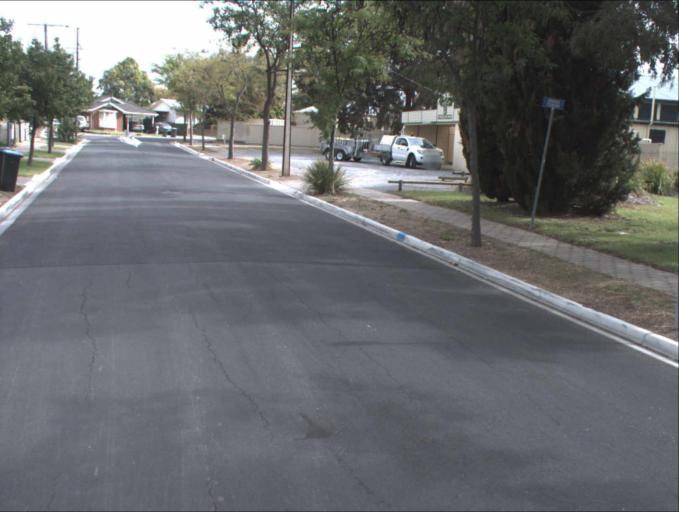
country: AU
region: South Australia
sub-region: Port Adelaide Enfield
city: Klemzig
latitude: -34.8652
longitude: 138.6388
